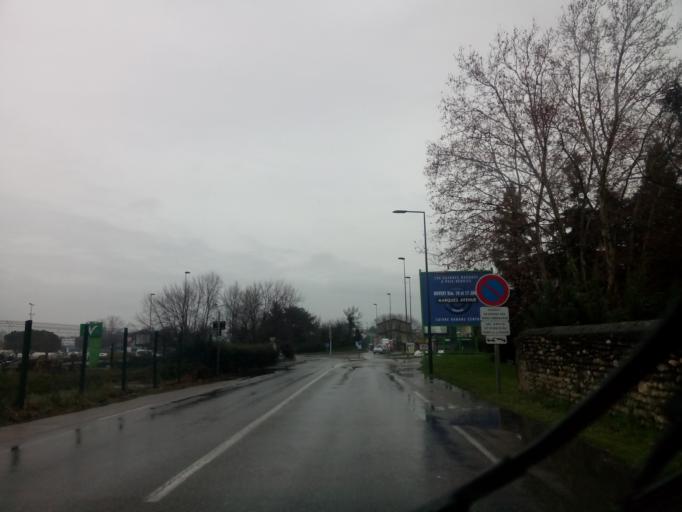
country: FR
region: Rhone-Alpes
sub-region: Departement de la Drome
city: Romans-sur-Isere
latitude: 45.0434
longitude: 5.0282
